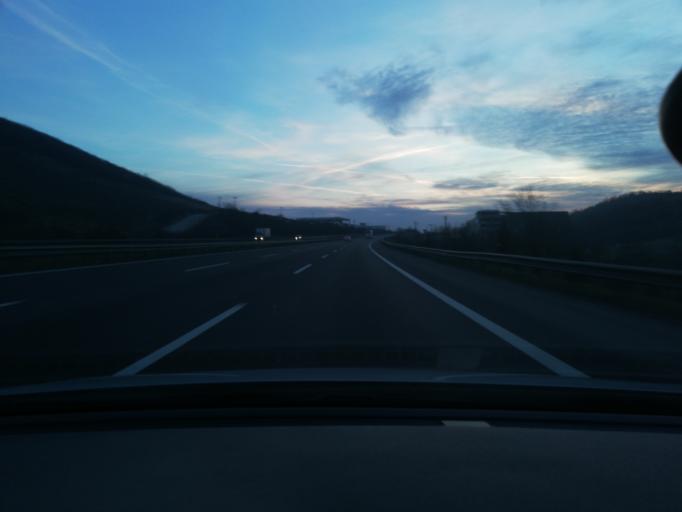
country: TR
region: Duzce
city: Gumusova
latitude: 40.8383
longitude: 30.9489
